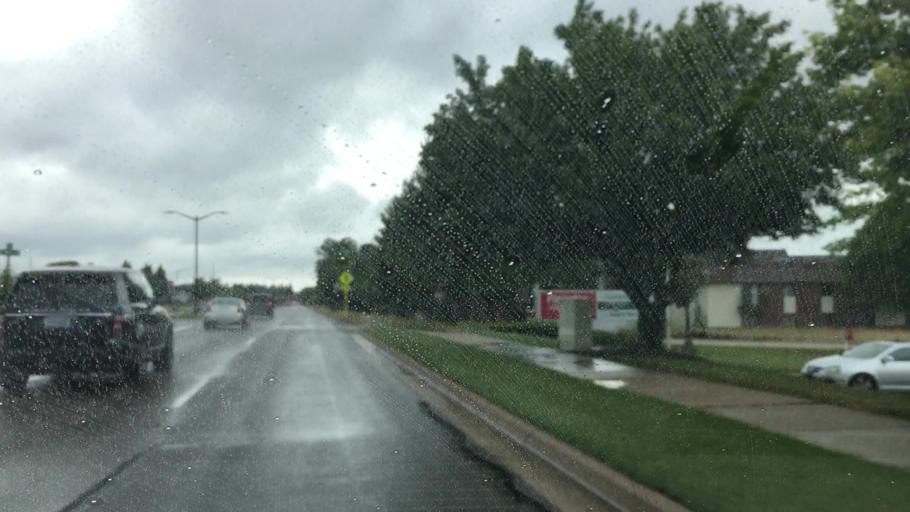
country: US
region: Michigan
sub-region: Ottawa County
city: Holland
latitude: 42.7834
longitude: -86.0714
